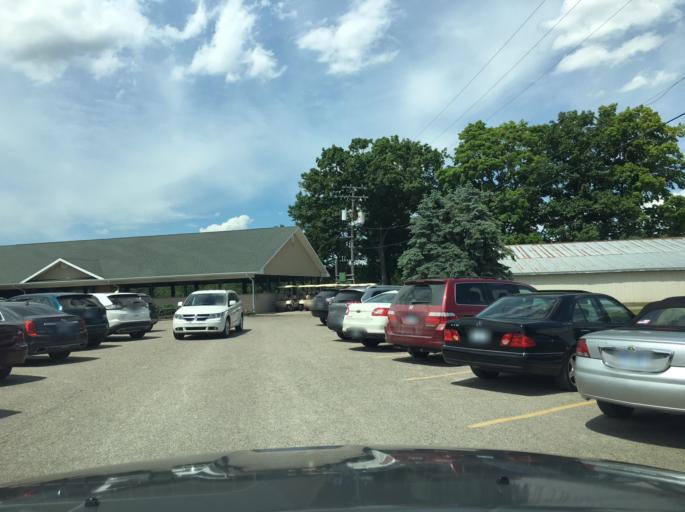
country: US
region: Michigan
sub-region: Macomb County
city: Romeo
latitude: 42.7906
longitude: -82.9590
